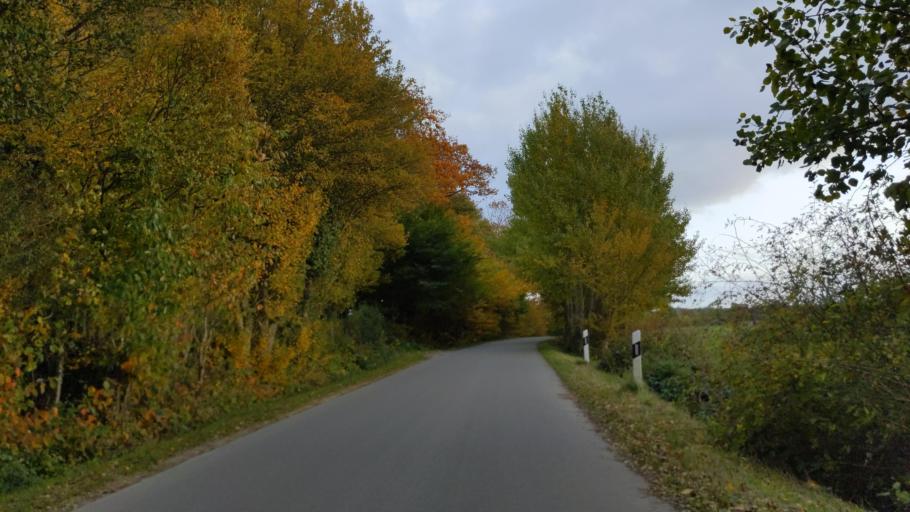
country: DE
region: Schleswig-Holstein
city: Kasseedorf
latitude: 54.1260
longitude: 10.7067
